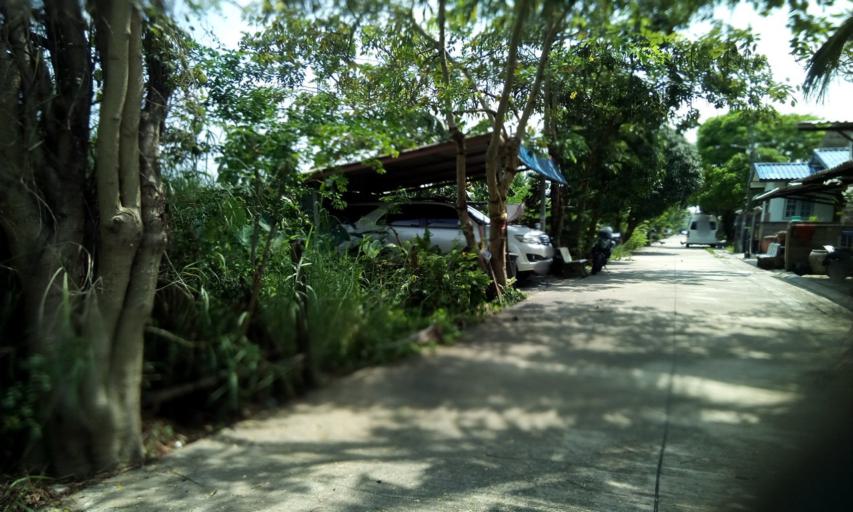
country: TH
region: Pathum Thani
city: Ban Rangsit
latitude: 14.0579
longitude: 100.8266
